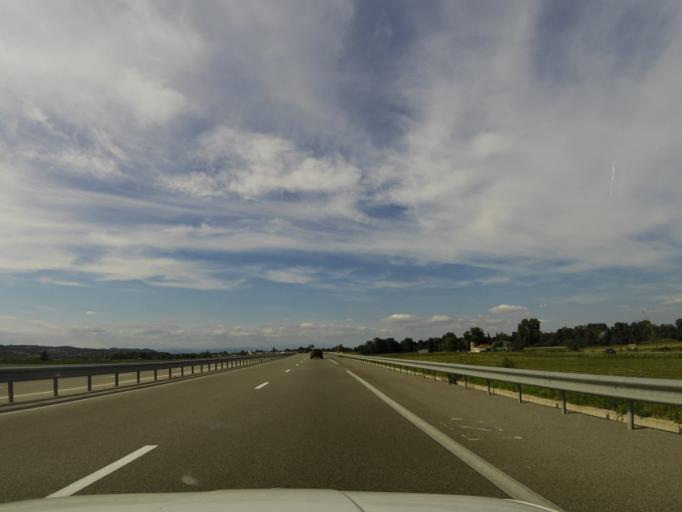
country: FR
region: Languedoc-Roussillon
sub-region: Departement du Gard
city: La Calmette
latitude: 43.9469
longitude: 4.2494
